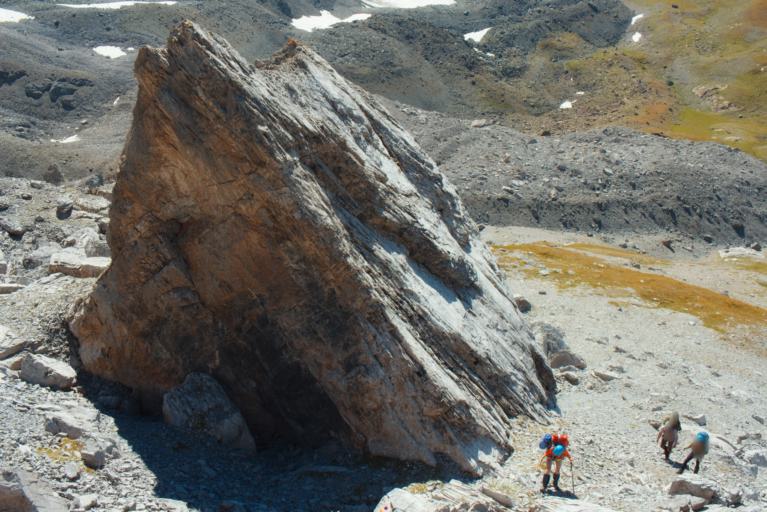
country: RU
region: Karachayevo-Cherkesiya
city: Nizhniy Arkhyz
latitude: 43.5945
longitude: 41.1843
